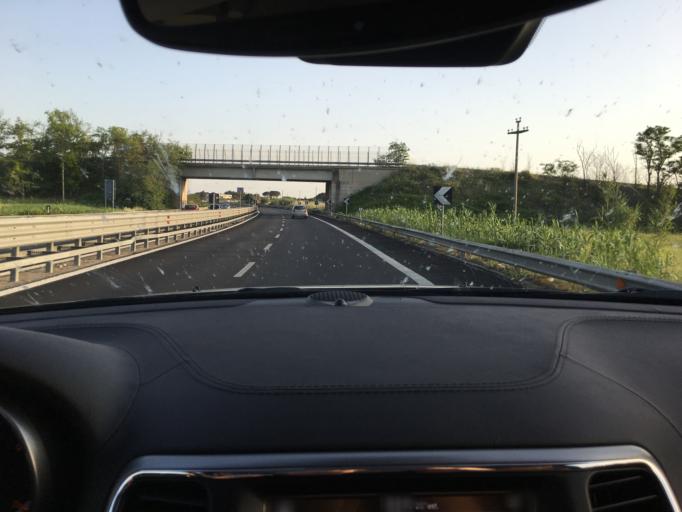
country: IT
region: Apulia
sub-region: Provincia di Lecce
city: San Pietro in Lama
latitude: 40.2997
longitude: 18.1324
